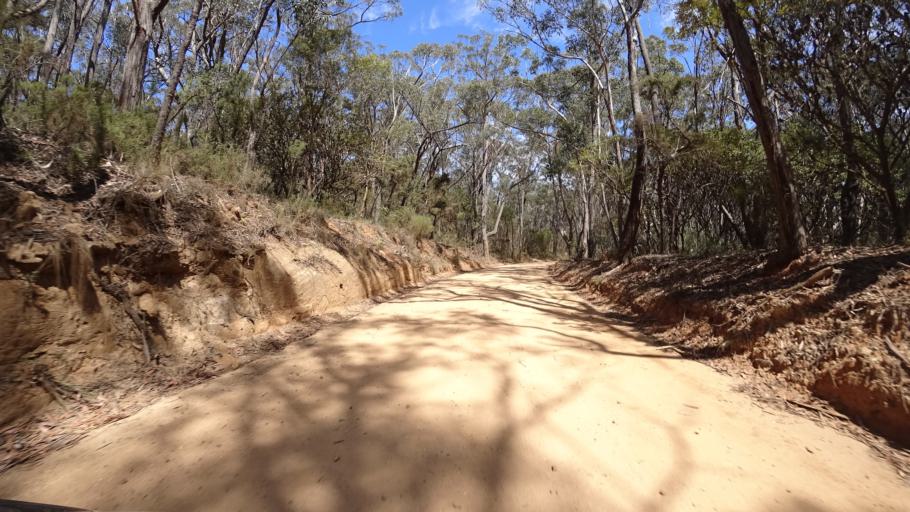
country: AU
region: New South Wales
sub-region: Lithgow
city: Lithgow
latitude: -33.2775
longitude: 150.2331
